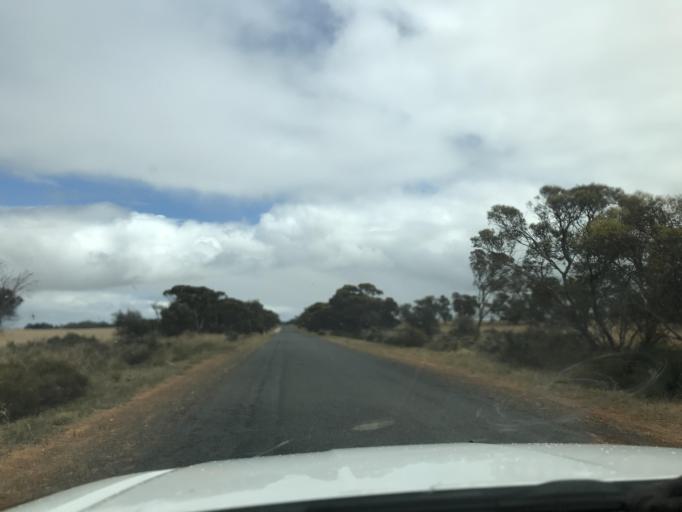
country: AU
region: South Australia
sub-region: Tatiara
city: Bordertown
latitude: -36.1443
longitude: 141.2306
